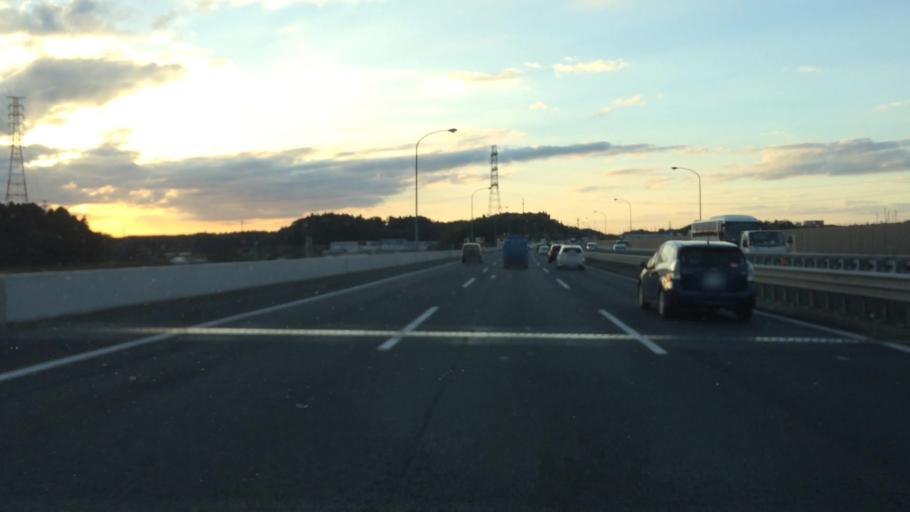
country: JP
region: Chiba
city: Sakura
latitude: 35.6821
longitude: 140.2028
